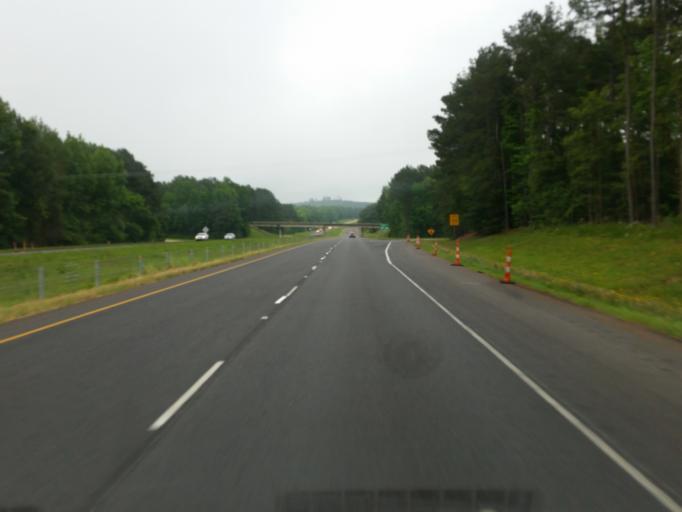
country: US
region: Louisiana
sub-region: Bienville Parish
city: Arcadia
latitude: 32.5632
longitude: -93.0585
